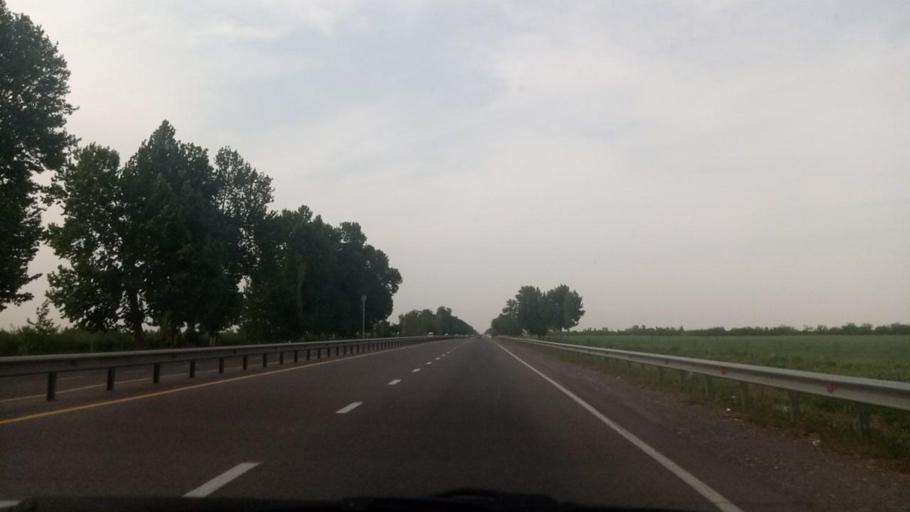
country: UZ
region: Toshkent Shahri
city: Bektemir
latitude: 41.1942
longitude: 69.4032
